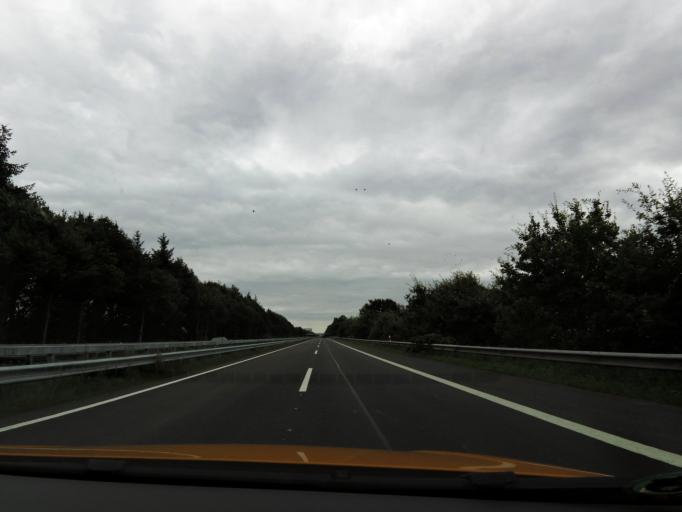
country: DE
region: Lower Saxony
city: Westerstede
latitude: 53.2726
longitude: 7.9195
